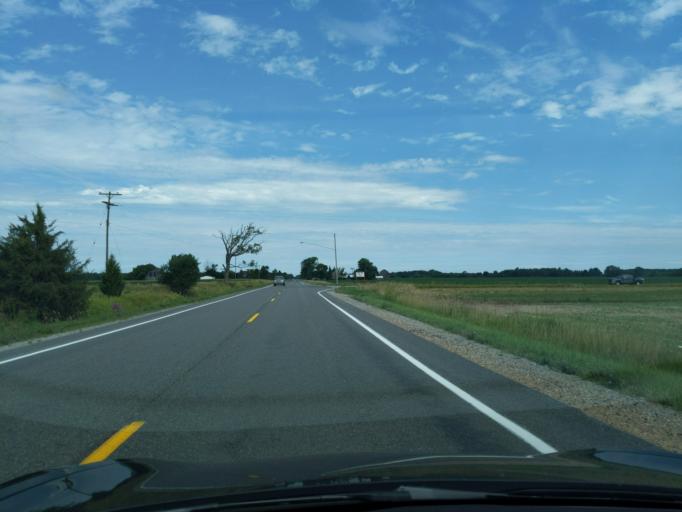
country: US
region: Michigan
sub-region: Gratiot County
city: Breckenridge
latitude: 43.4955
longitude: -84.3698
